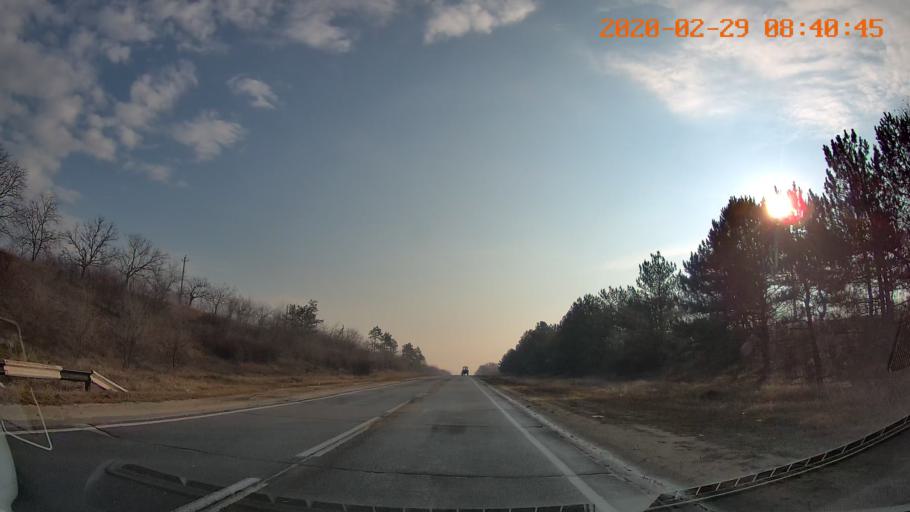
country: MD
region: Anenii Noi
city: Varnita
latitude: 46.9236
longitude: 29.4240
